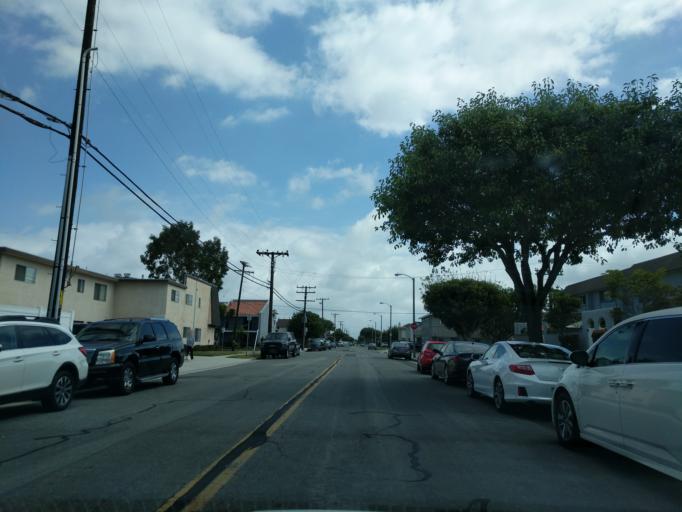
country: US
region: California
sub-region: Orange County
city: Westminster
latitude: 33.7189
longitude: -118.0487
